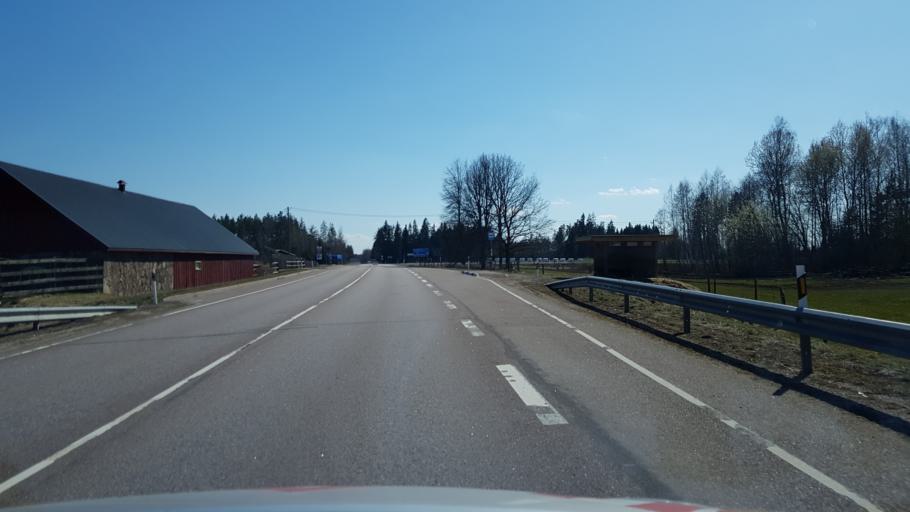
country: EE
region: Jogevamaa
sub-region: Mustvee linn
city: Mustvee
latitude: 58.7077
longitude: 26.8180
